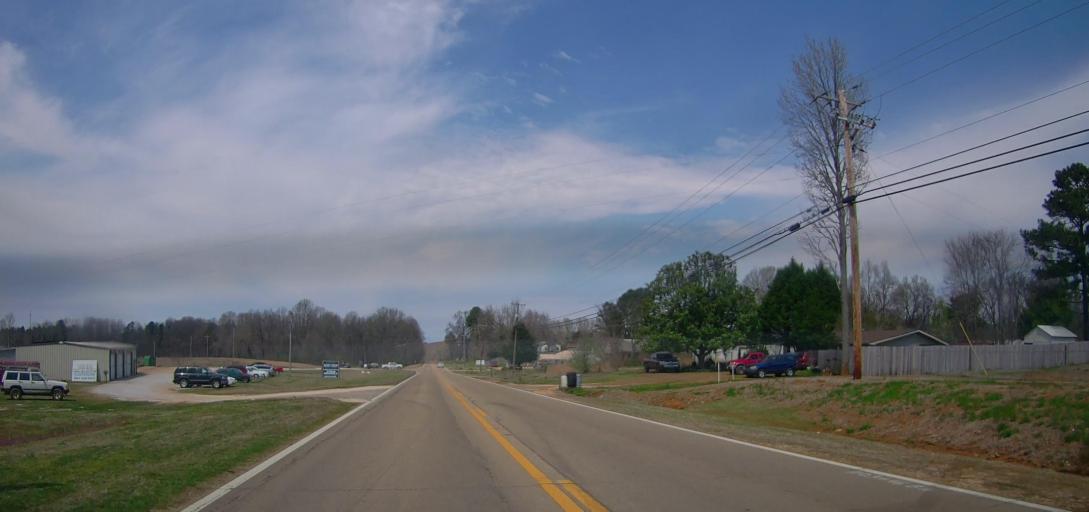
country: US
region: Mississippi
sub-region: Union County
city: New Albany
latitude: 34.4576
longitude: -88.9764
